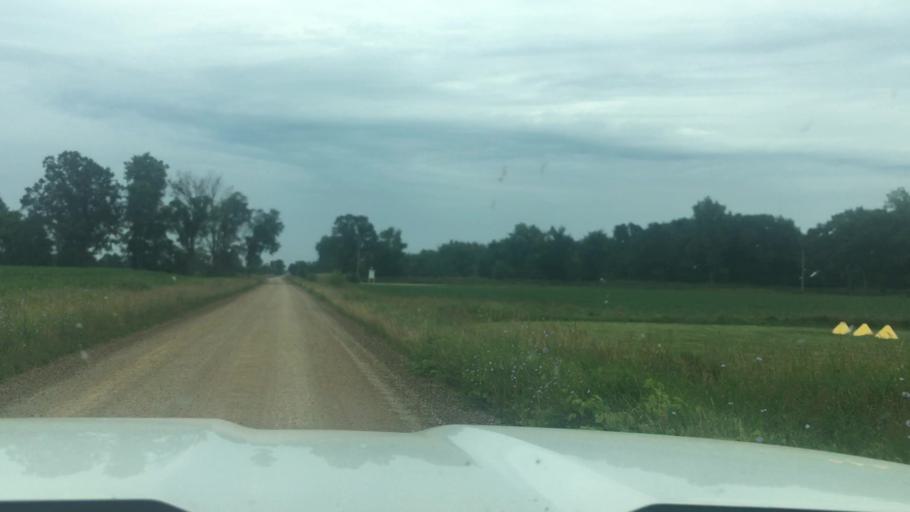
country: US
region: Michigan
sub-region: Clinton County
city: Saint Johns
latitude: 43.0655
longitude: -84.4841
